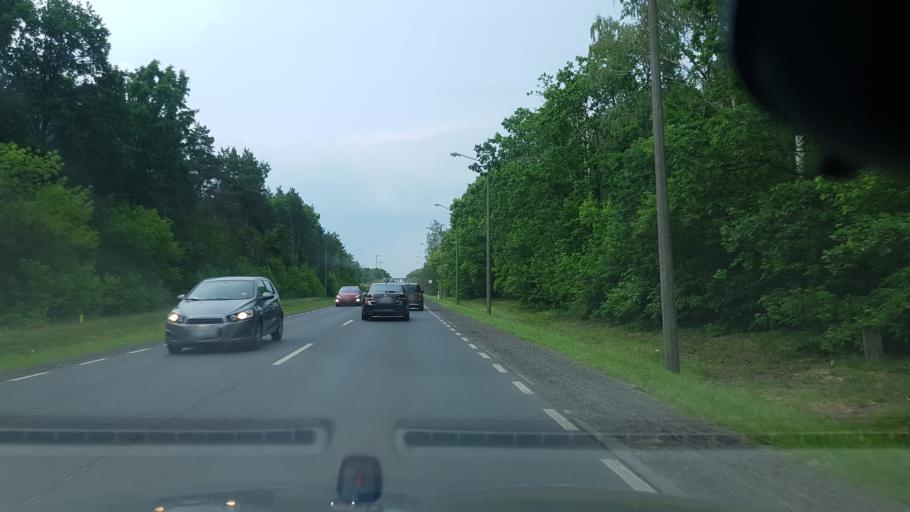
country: PL
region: Masovian Voivodeship
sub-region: Powiat legionowski
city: Michalow-Reginow
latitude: 52.4327
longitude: 20.9859
